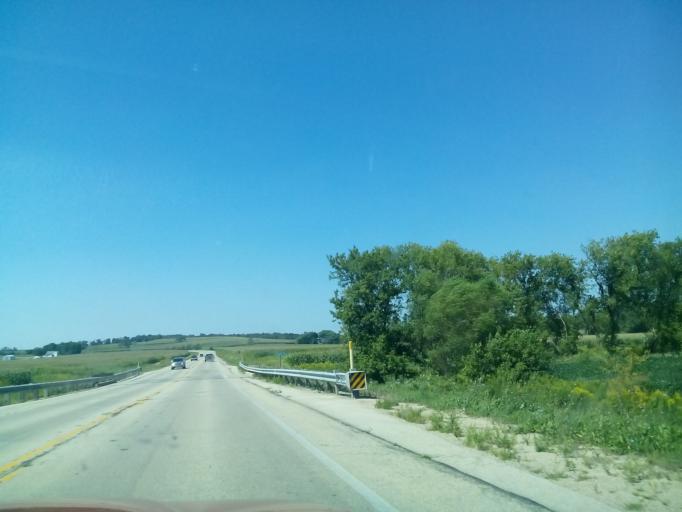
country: US
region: Wisconsin
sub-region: Green County
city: Monticello
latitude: 42.7112
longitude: -89.6074
